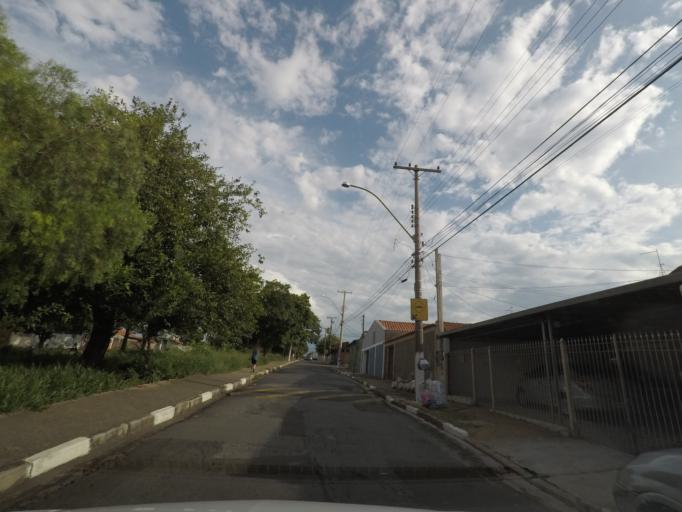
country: BR
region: Sao Paulo
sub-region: Campinas
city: Campinas
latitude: -22.9095
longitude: -47.1191
